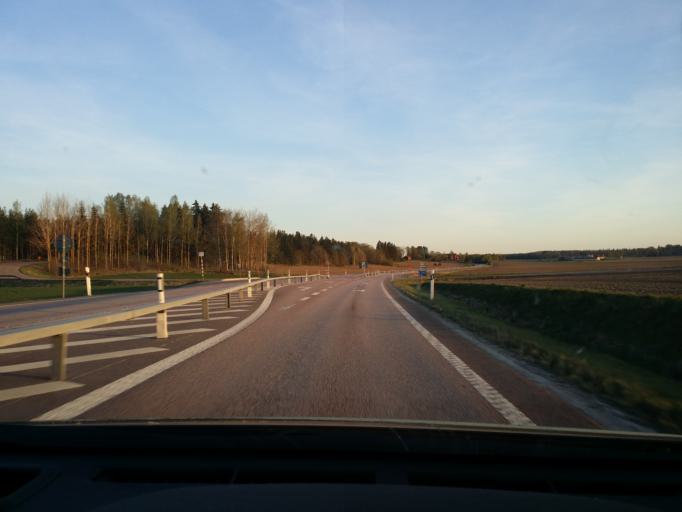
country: SE
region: Vaestmanland
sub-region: Vasteras
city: Tillberga
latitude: 59.7096
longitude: 16.5832
